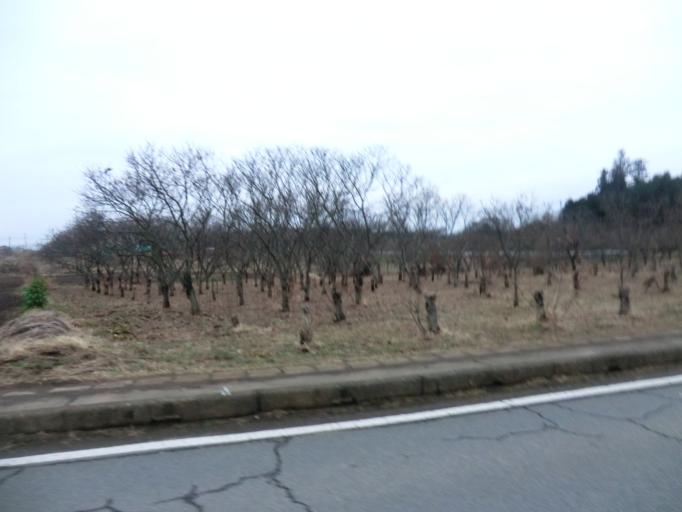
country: JP
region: Ibaraki
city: Naka
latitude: 36.0984
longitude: 140.1248
